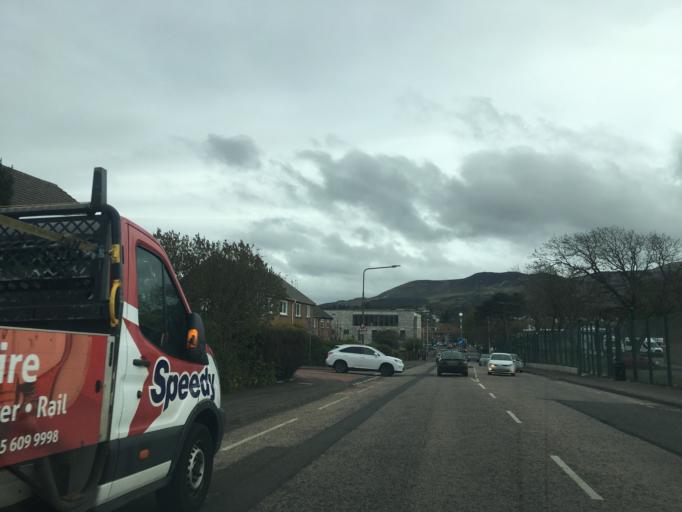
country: GB
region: Scotland
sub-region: Edinburgh
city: Colinton
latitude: 55.9133
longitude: -3.2389
